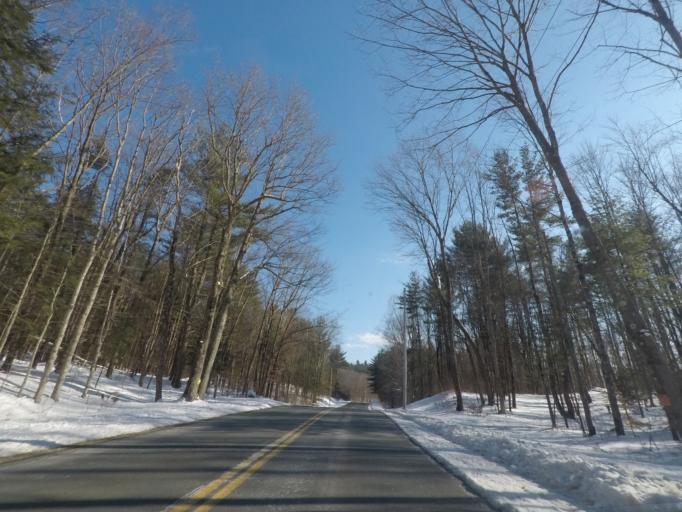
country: US
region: New York
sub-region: Rensselaer County
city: Hoosick Falls
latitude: 42.8927
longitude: -73.4963
